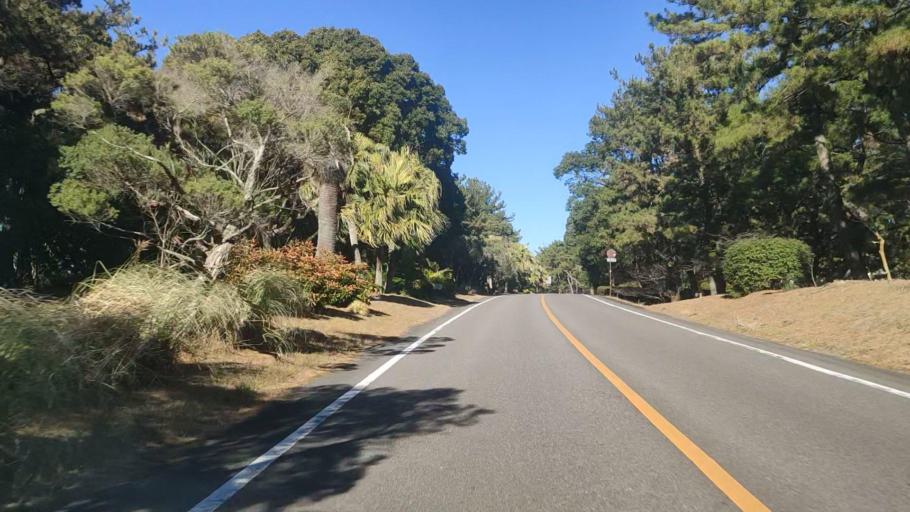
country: JP
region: Miyazaki
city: Miyazaki-shi
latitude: 31.9523
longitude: 131.4667
